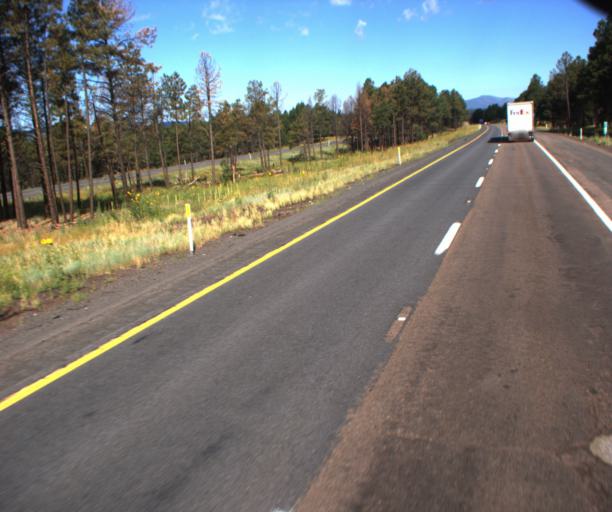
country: US
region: Arizona
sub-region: Coconino County
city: Flagstaff
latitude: 35.2225
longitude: -111.7937
